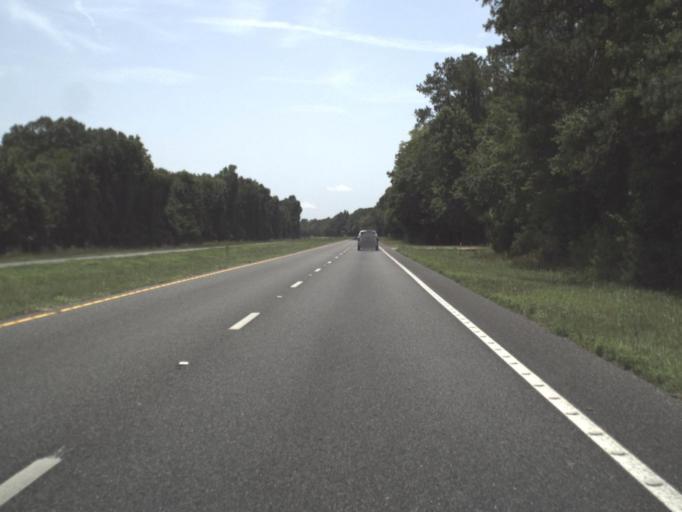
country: US
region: Florida
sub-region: Taylor County
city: Perry
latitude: 29.9366
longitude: -83.4471
